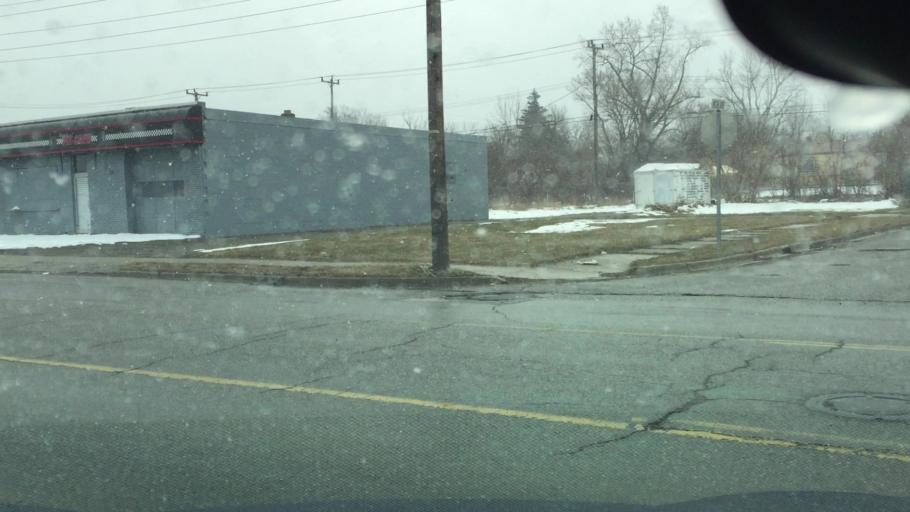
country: US
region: Michigan
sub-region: Oakland County
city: Pontiac
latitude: 42.6194
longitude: -83.2855
